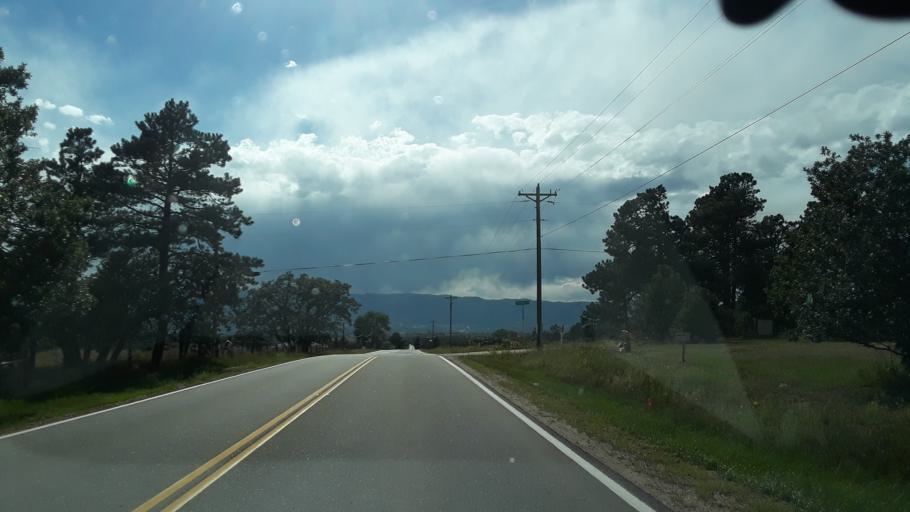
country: US
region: Colorado
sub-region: El Paso County
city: Black Forest
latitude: 39.0128
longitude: -104.7515
